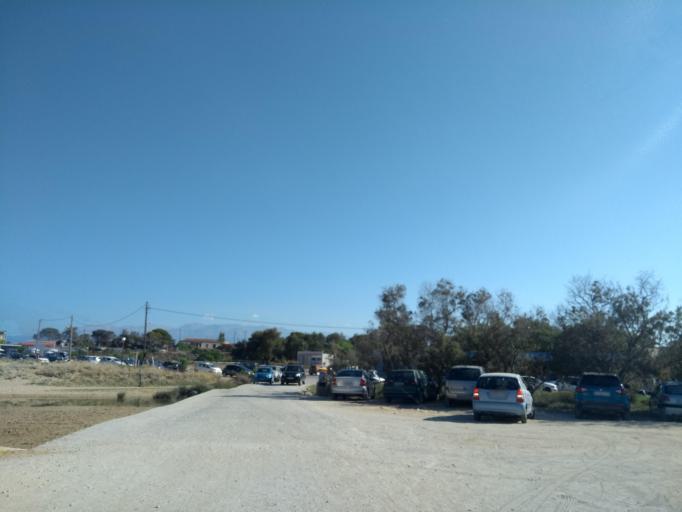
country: GR
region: Crete
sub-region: Nomos Chanias
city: Pithari
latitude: 35.5923
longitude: 24.0949
